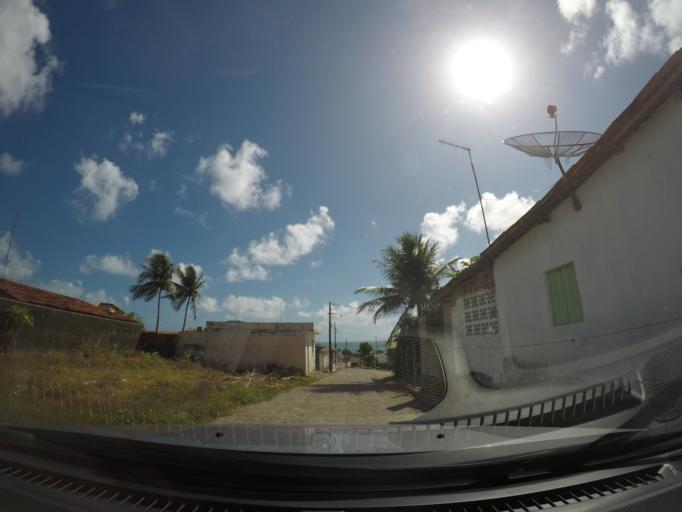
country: BR
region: Paraiba
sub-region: Pitimbu
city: Pitimbu
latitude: -7.4729
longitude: -34.8111
